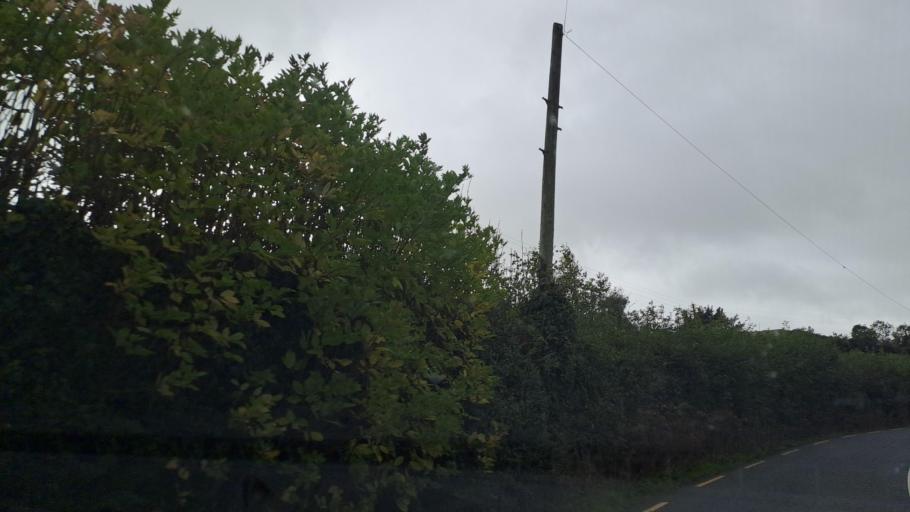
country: IE
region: Ulster
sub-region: An Cabhan
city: Bailieborough
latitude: 53.9604
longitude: -6.9256
